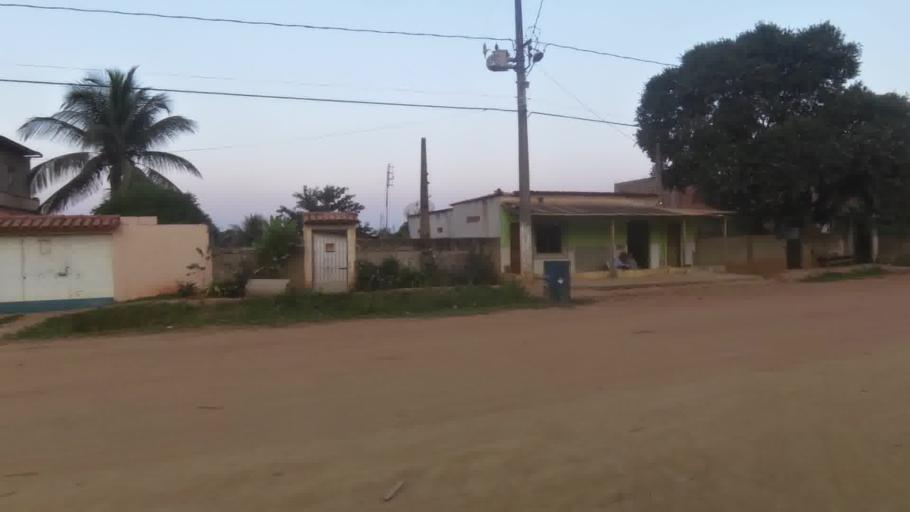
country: BR
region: Espirito Santo
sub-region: Piuma
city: Piuma
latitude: -20.8265
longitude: -40.7205
